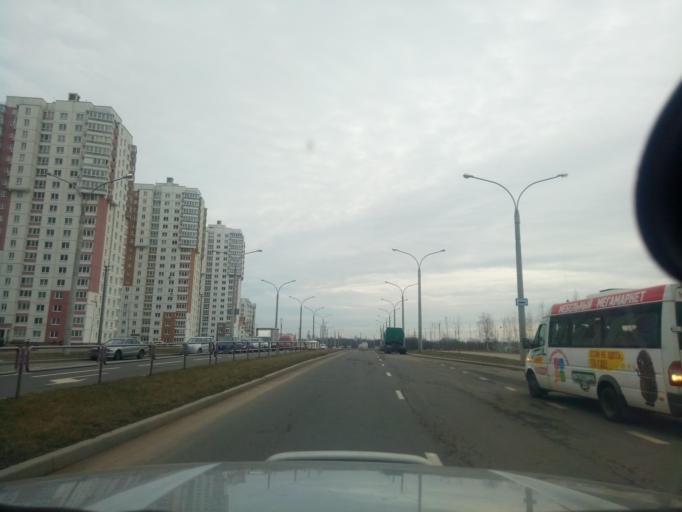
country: BY
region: Minsk
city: Syenitsa
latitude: 53.8355
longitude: 27.5887
